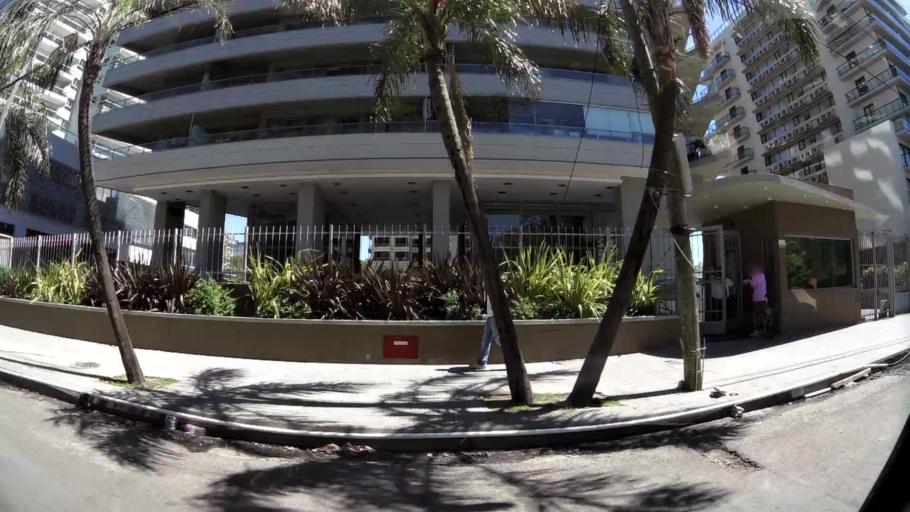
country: AR
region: Buenos Aires
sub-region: Partido de Vicente Lopez
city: Olivos
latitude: -34.5079
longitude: -58.4782
